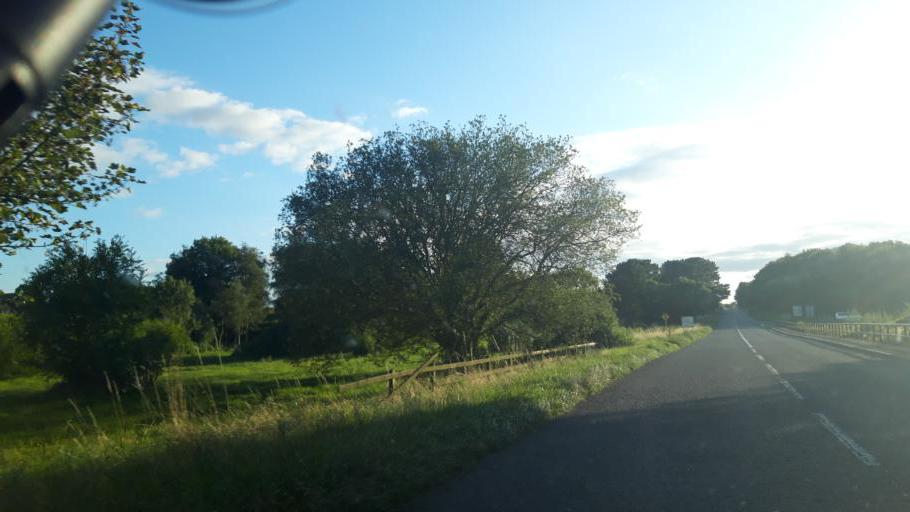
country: IE
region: Leinster
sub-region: Lu
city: Carlingford
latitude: 54.0210
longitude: -6.1427
